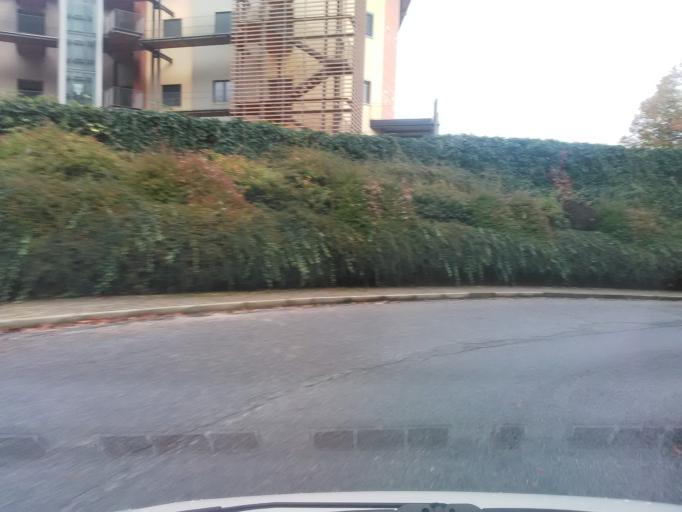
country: IT
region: Piedmont
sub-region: Provincia di Novara
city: Pella
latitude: 45.7995
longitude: 8.3763
